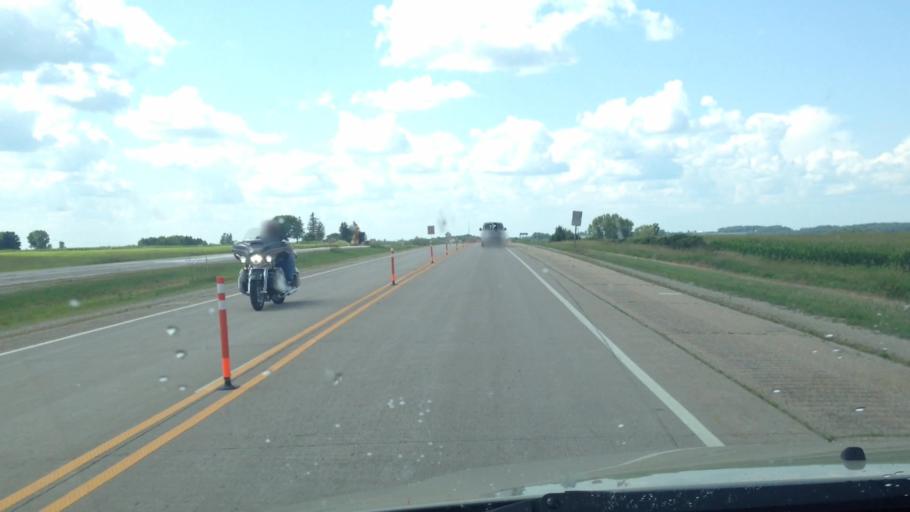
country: US
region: Wisconsin
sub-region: Shawano County
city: Bonduel
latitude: 44.6995
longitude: -88.3585
